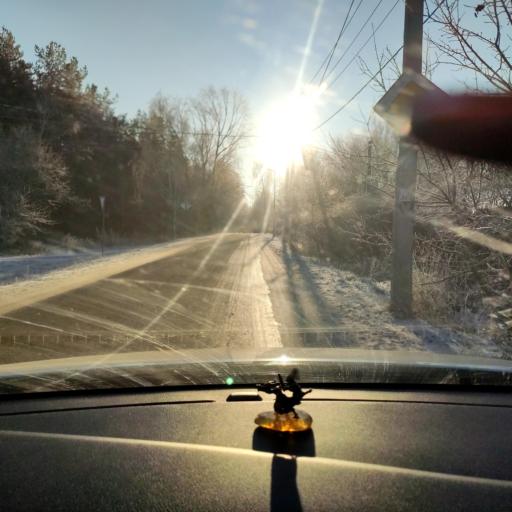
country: RU
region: Tatarstan
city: Stolbishchi
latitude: 55.6750
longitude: 49.1174
